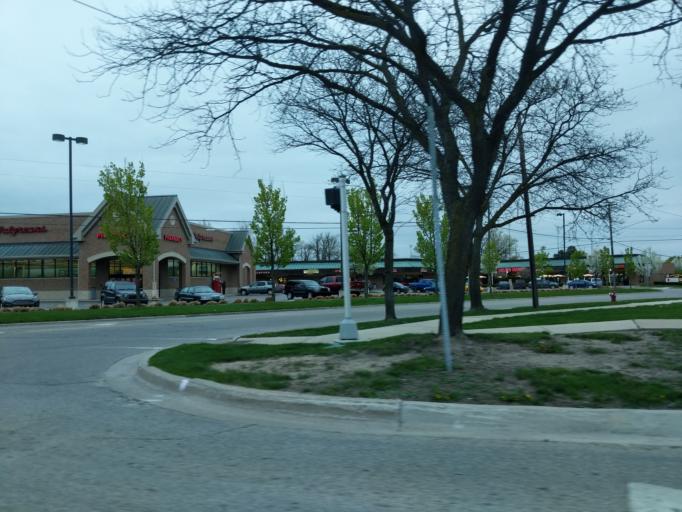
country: US
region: Michigan
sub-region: Midland County
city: Midland
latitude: 43.6192
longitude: -84.2191
